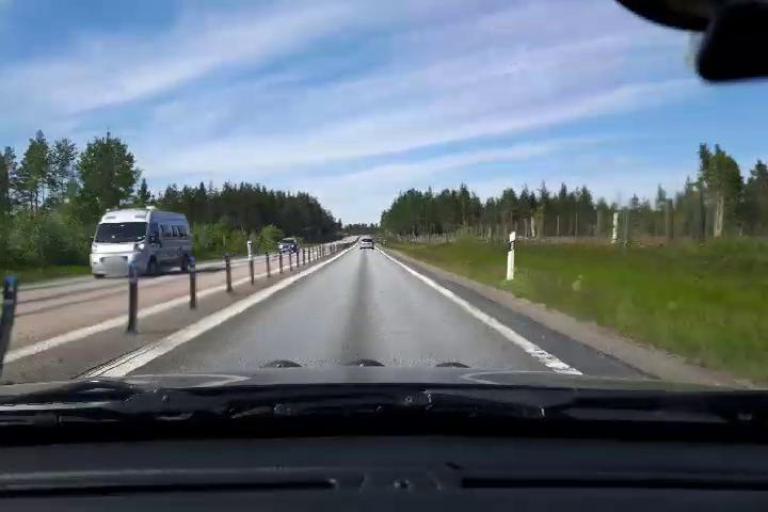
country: SE
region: Gaevleborg
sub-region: Gavle Kommun
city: Norrsundet
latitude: 60.9749
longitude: 17.0217
